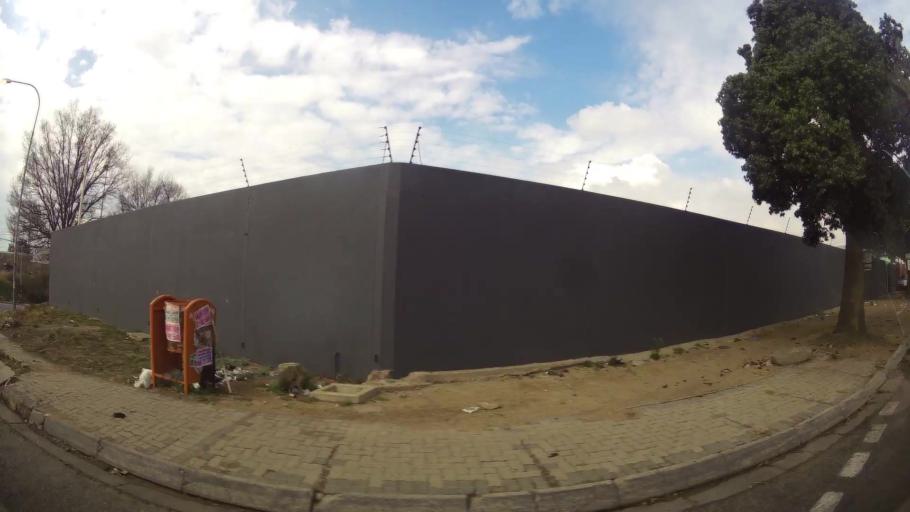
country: ZA
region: Gauteng
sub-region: Sedibeng District Municipality
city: Vereeniging
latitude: -26.6810
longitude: 27.9324
